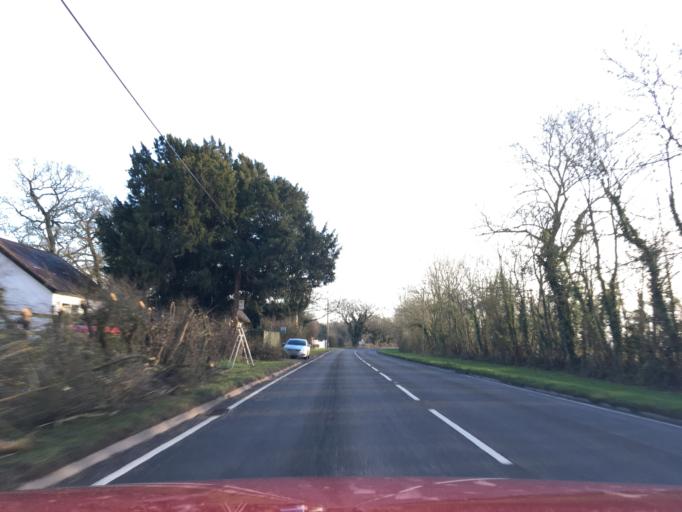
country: GB
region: England
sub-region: Warwickshire
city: Henley in Arden
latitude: 52.2569
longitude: -1.7625
